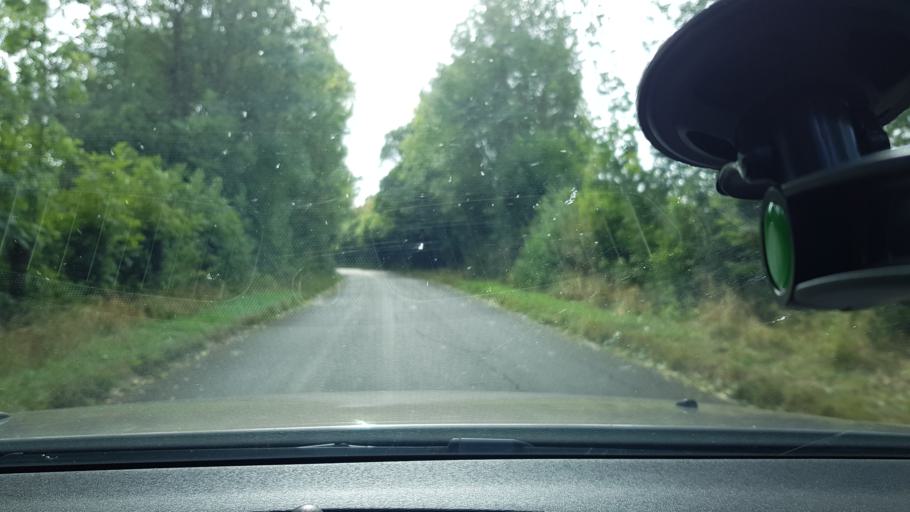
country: GB
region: England
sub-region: Wiltshire
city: Chilton Foliat
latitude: 51.4634
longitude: -1.5009
